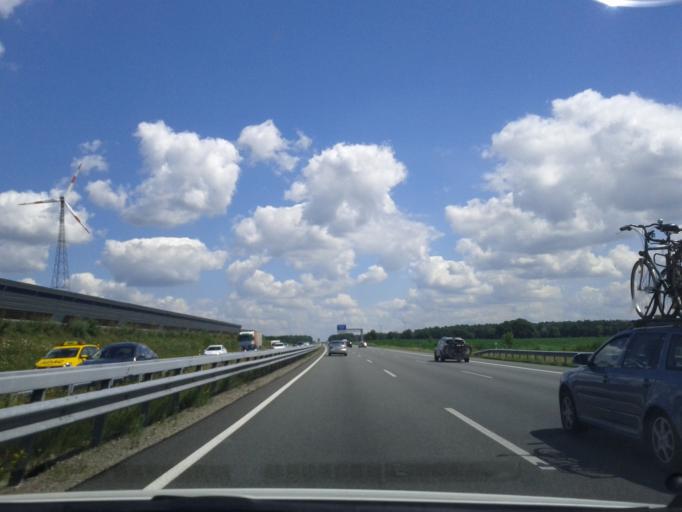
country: DE
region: Lower Saxony
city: Ottersberg
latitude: 53.0614
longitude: 9.1016
